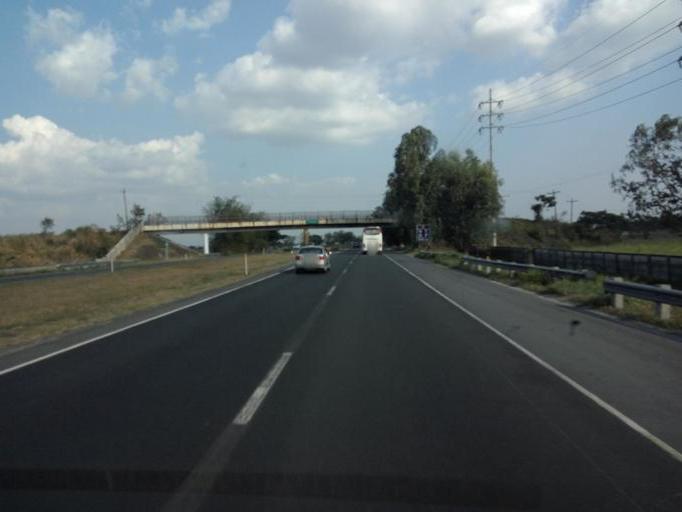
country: PH
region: Central Luzon
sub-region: Province of Pampanga
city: Acli
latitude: 15.1331
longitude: 120.6405
